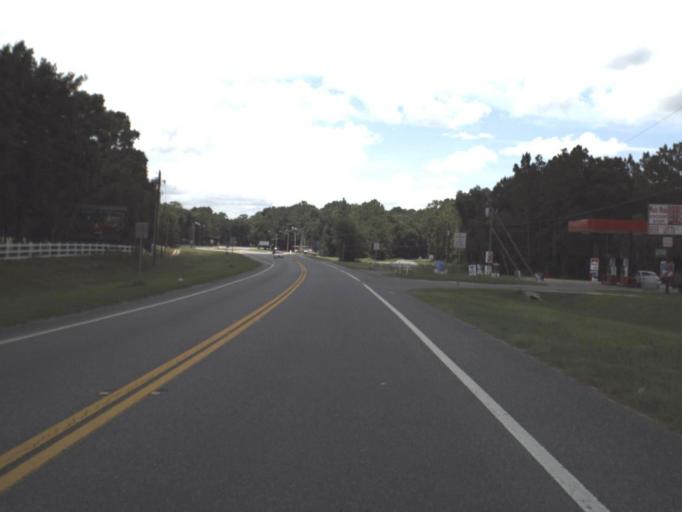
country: US
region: Florida
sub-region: Suwannee County
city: Live Oak
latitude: 30.3872
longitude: -82.9385
